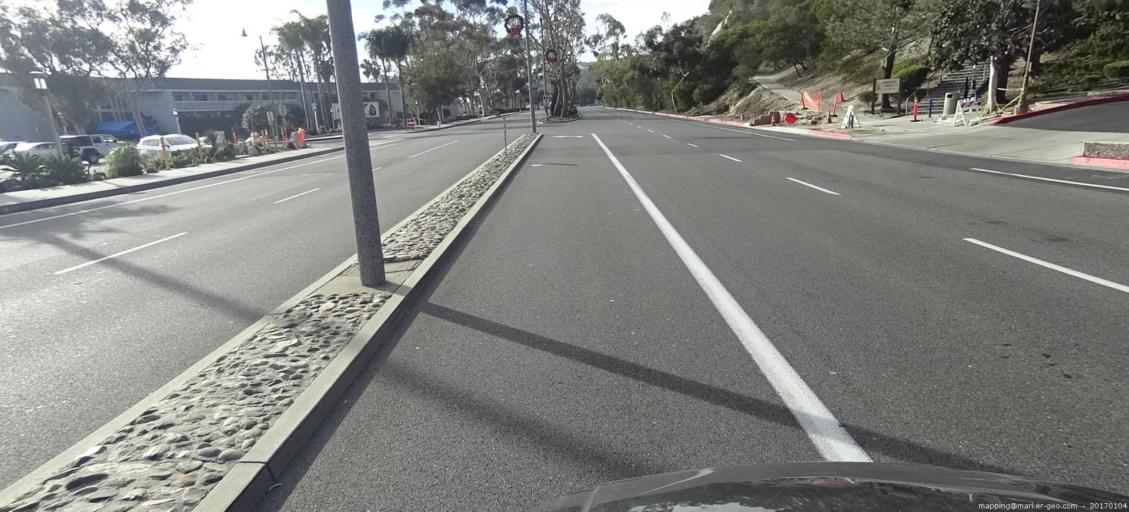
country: US
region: California
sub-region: Orange County
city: Dana Point
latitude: 33.4625
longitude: -117.6951
